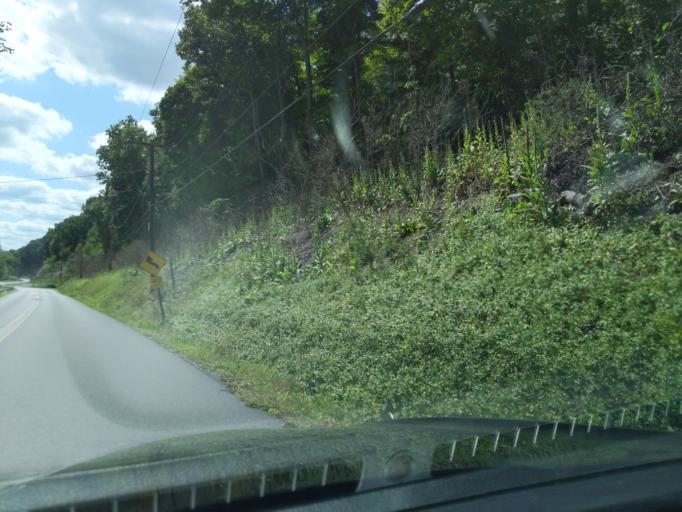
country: US
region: Pennsylvania
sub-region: Blair County
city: Tyrone
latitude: 40.6994
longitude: -78.2252
